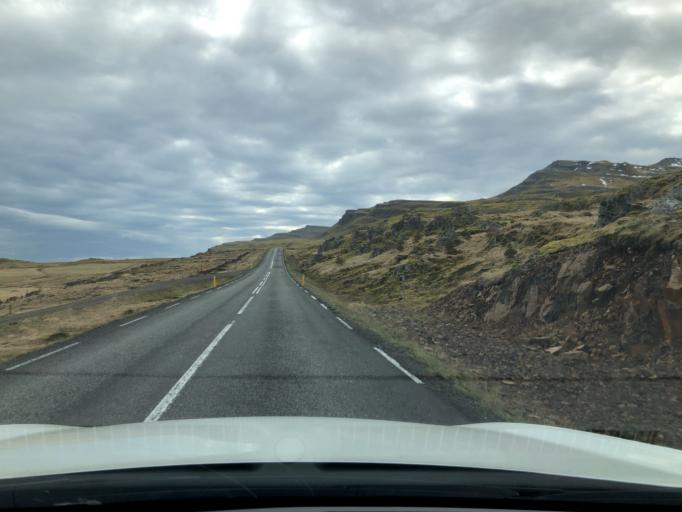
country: IS
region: East
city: Eskifjoerdur
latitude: 64.8925
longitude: -13.8460
